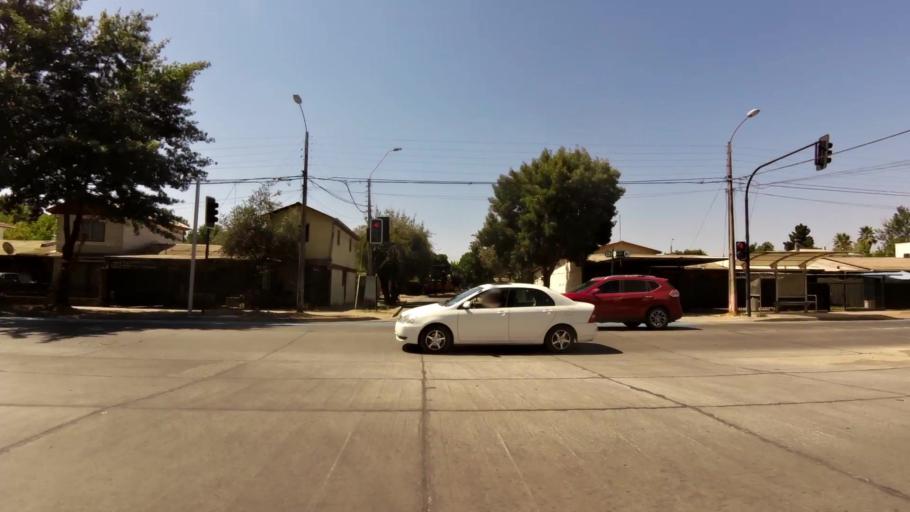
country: CL
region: Maule
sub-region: Provincia de Talca
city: Talca
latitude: -35.4120
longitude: -71.6567
